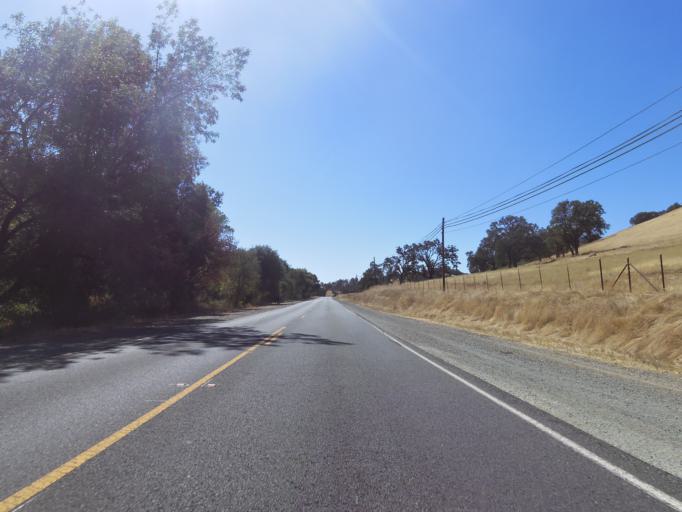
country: US
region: California
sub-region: Amador County
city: Plymouth
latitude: 38.5002
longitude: -120.8480
